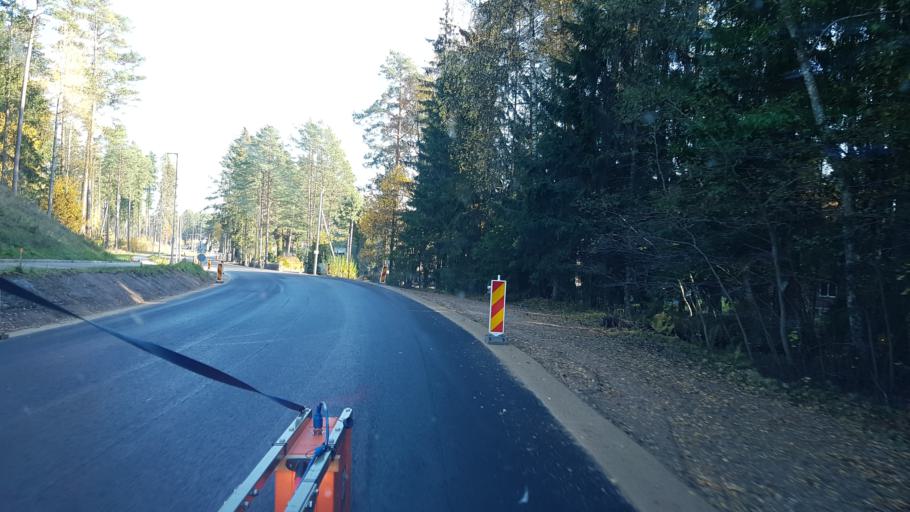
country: EE
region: Vorumaa
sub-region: Antsla vald
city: Vana-Antsla
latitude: 57.8312
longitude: 26.5123
